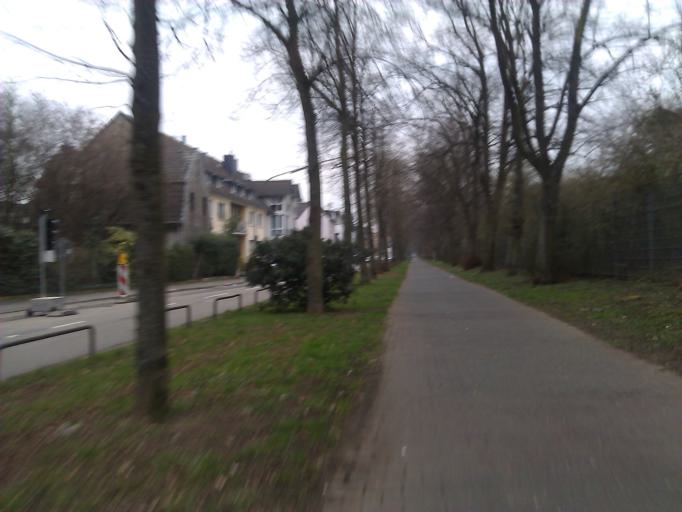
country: DE
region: North Rhine-Westphalia
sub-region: Regierungsbezirk Koln
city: Riehl
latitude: 50.9860
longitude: 6.9666
